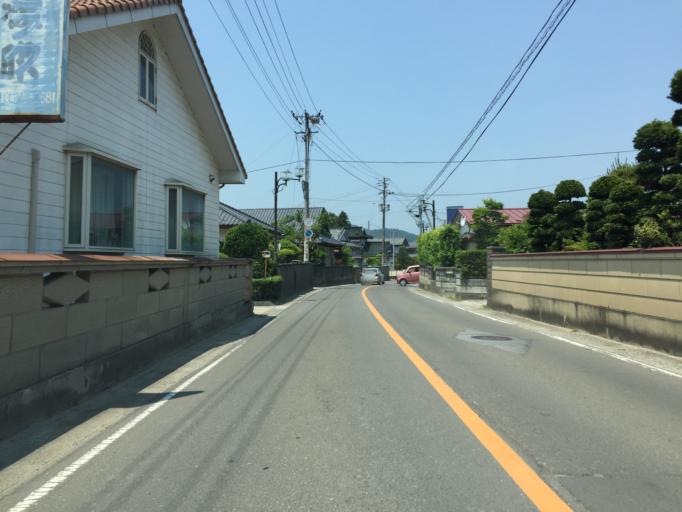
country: JP
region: Miyagi
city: Marumori
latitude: 37.8653
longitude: 140.8280
